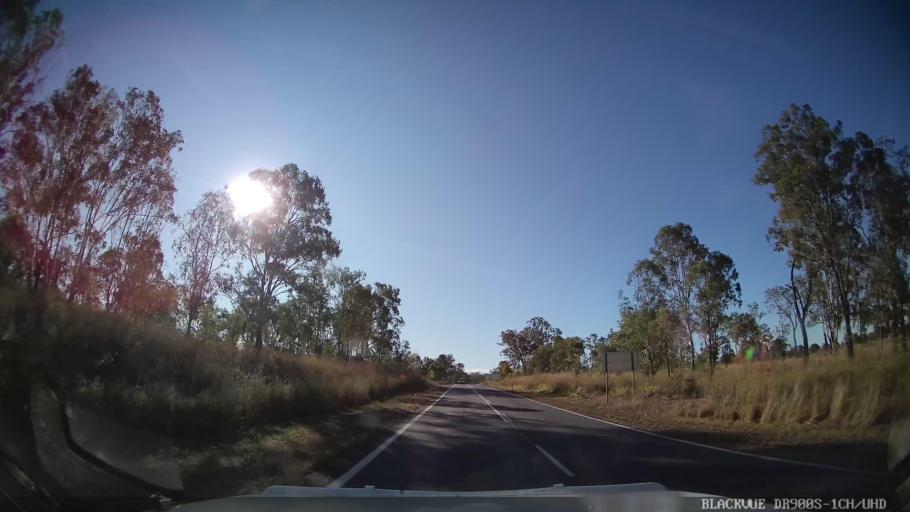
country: AU
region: Queensland
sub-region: Bundaberg
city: Sharon
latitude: -24.8263
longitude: 151.7071
